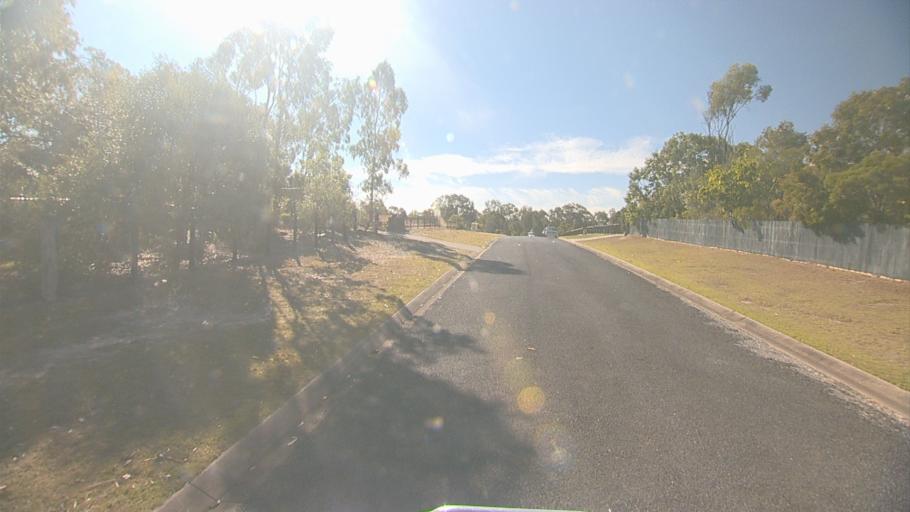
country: AU
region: Queensland
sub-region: Ipswich
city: Springfield Lakes
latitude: -27.7298
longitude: 152.9419
